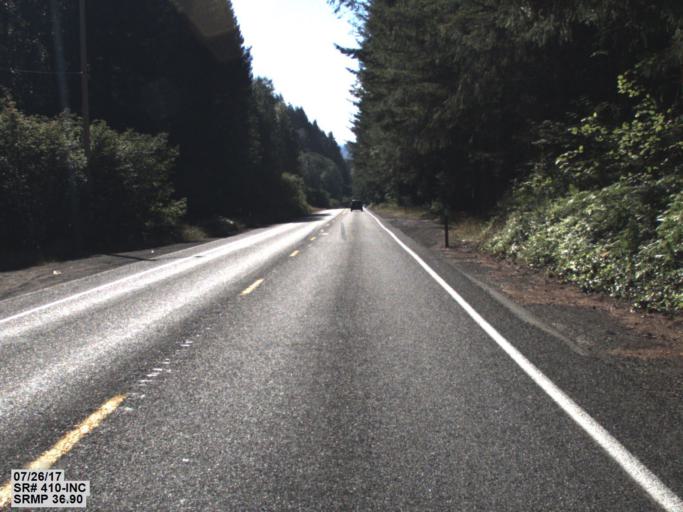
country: US
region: Washington
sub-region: King County
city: Enumclaw
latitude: 47.1714
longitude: -121.7705
